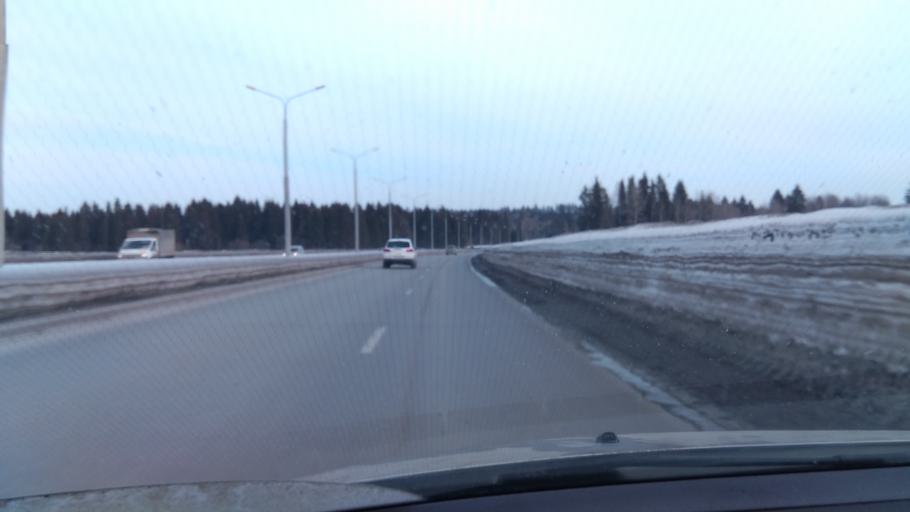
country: RU
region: Perm
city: Perm
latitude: 58.0059
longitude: 56.3612
